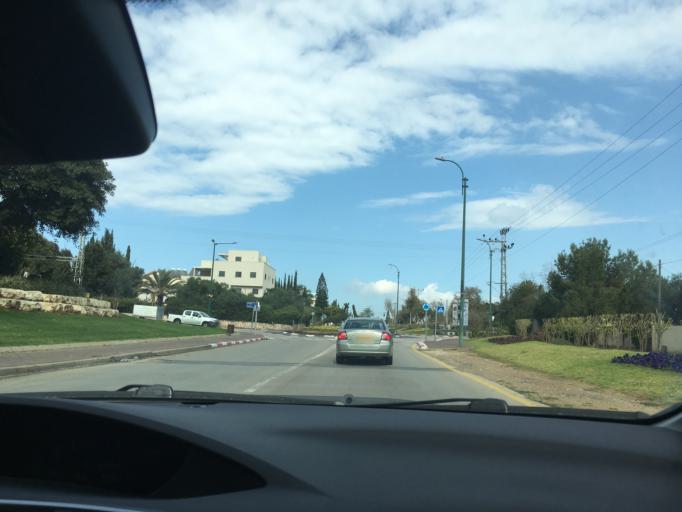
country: IL
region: Tel Aviv
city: Ramat HaSharon
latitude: 32.1651
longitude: 34.8530
